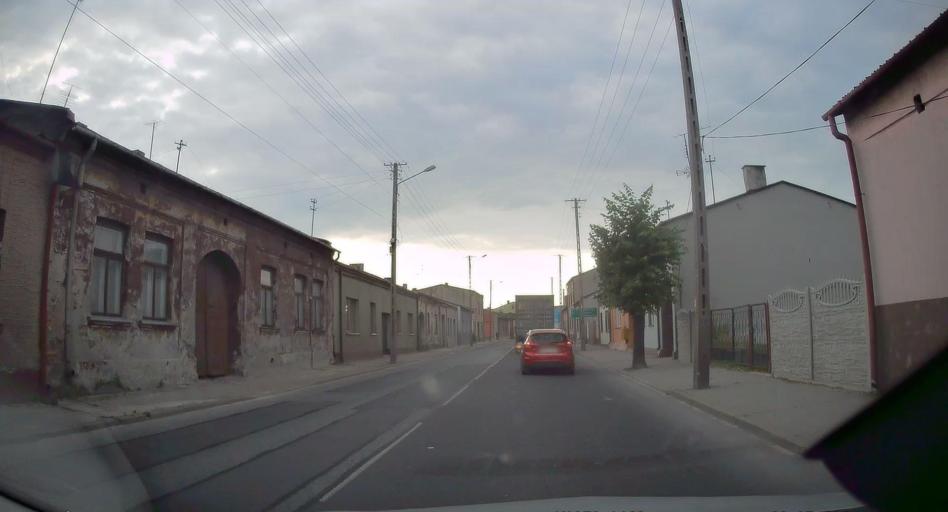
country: PL
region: Lodz Voivodeship
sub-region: Powiat radomszczanski
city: Kamiensk
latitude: 51.2021
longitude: 19.4990
